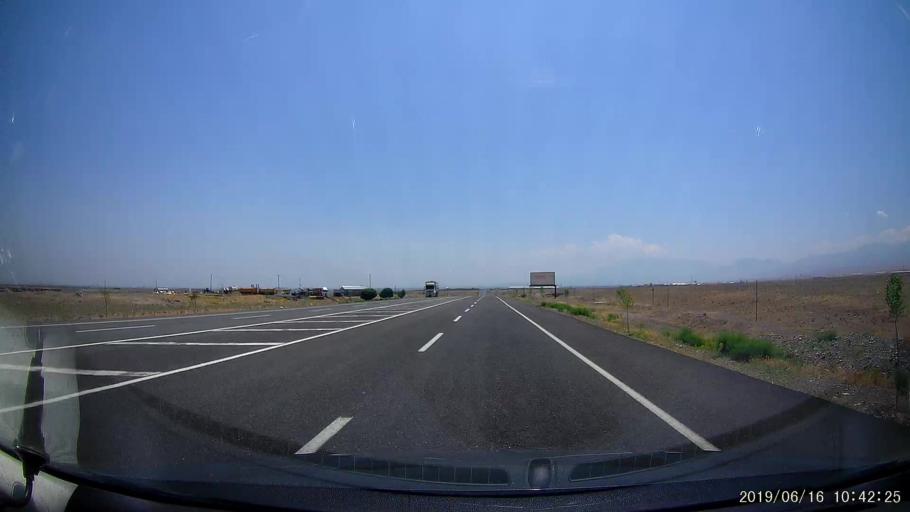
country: AM
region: Armavir
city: Shenavan
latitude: 40.0422
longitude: 43.8062
